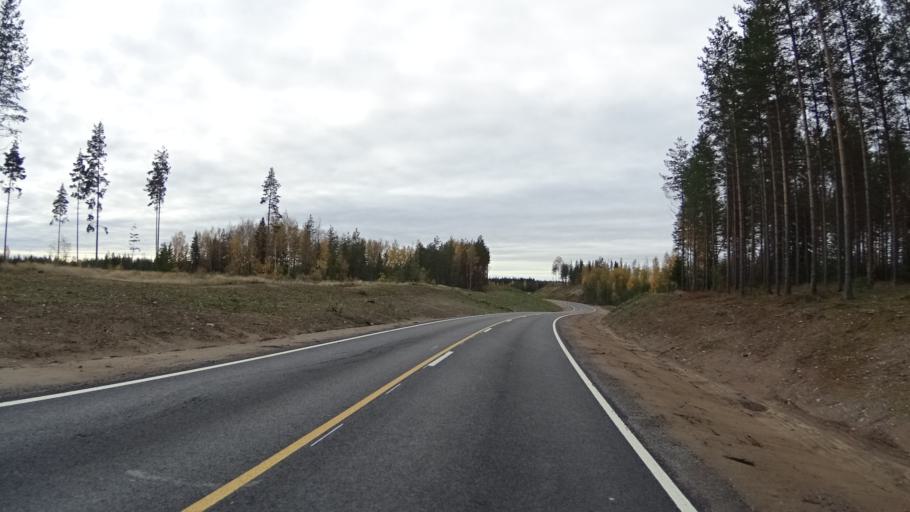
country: FI
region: South Karelia
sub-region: Lappeenranta
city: Taipalsaari
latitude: 61.0166
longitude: 27.9965
